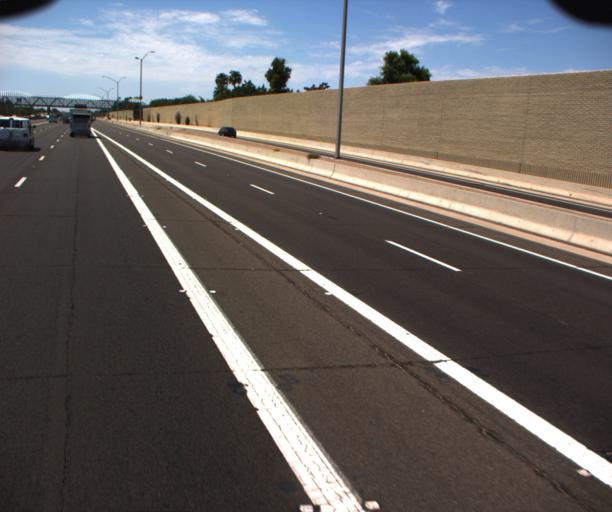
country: US
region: Arizona
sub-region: Maricopa County
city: Tempe
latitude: 33.3859
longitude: -111.8971
